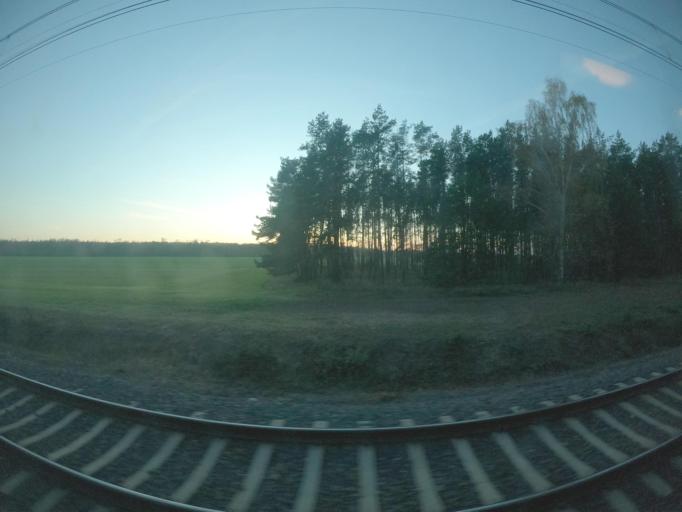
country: PL
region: West Pomeranian Voivodeship
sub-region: Powiat mysliborski
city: Boleszkowice
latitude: 52.7320
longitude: 14.5217
